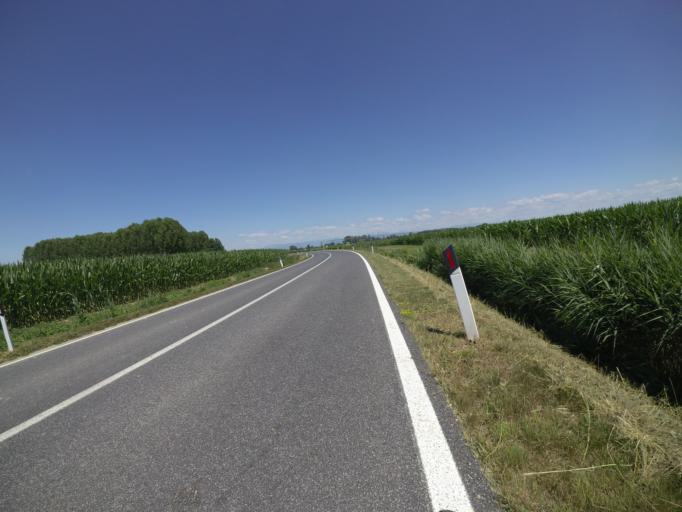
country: IT
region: Friuli Venezia Giulia
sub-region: Provincia di Udine
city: Rivignano
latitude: 45.8951
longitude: 13.0815
